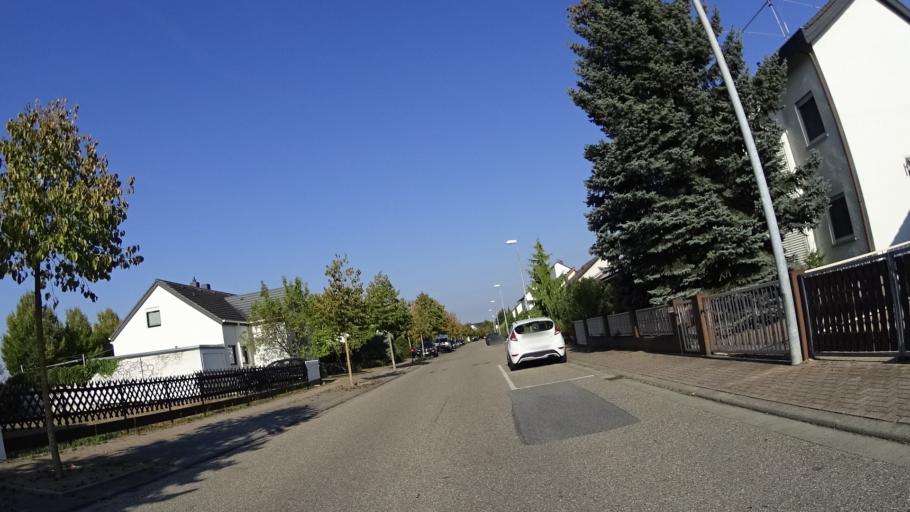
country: DE
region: Rheinland-Pfalz
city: Speyer
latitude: 49.3029
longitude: 8.4285
